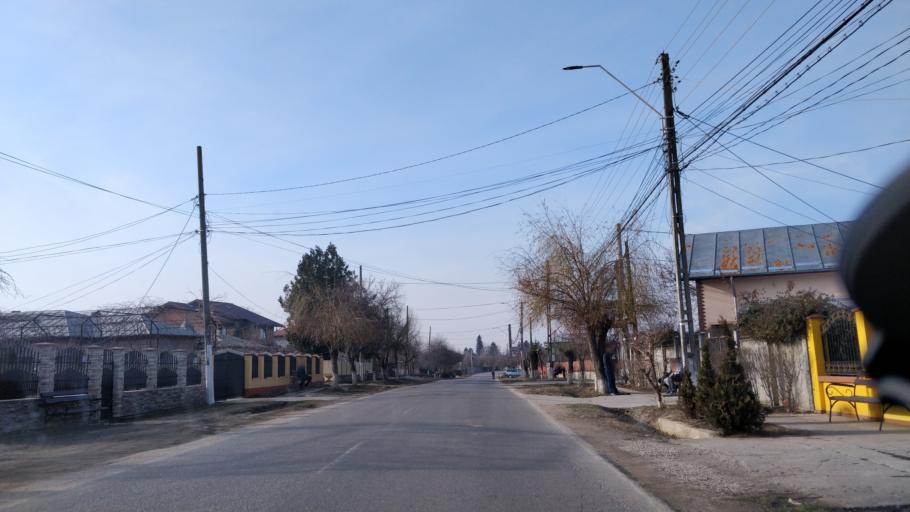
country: RO
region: Giurgiu
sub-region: Comuna Ulmi
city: Ulmi
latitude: 44.4951
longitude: 25.7741
